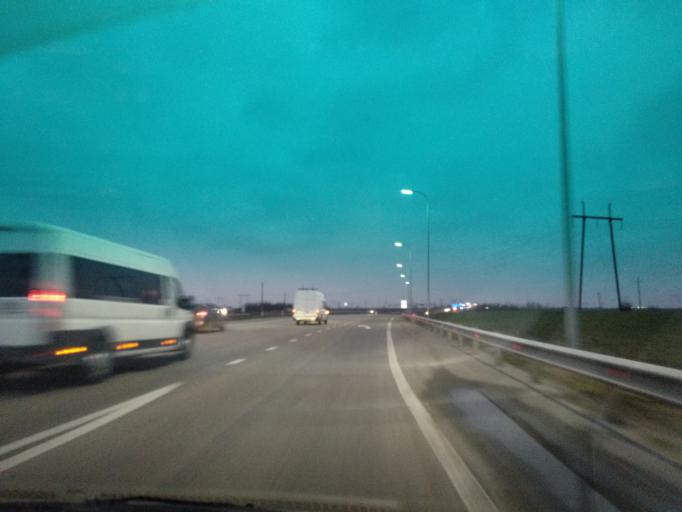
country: RU
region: Adygeya
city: Adygeysk
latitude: 44.8671
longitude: 39.1894
